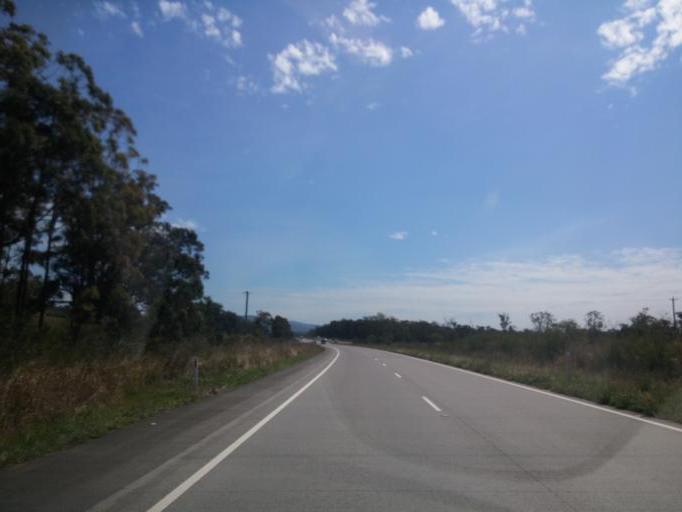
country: AU
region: New South Wales
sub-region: Great Lakes
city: Bulahdelah
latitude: -32.4527
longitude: 152.1976
